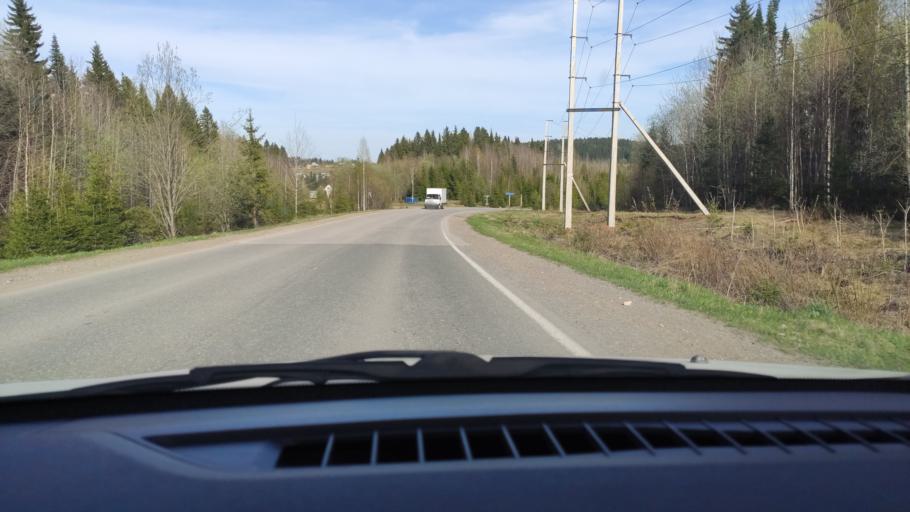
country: RU
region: Perm
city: Novyye Lyady
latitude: 57.9408
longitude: 56.6204
